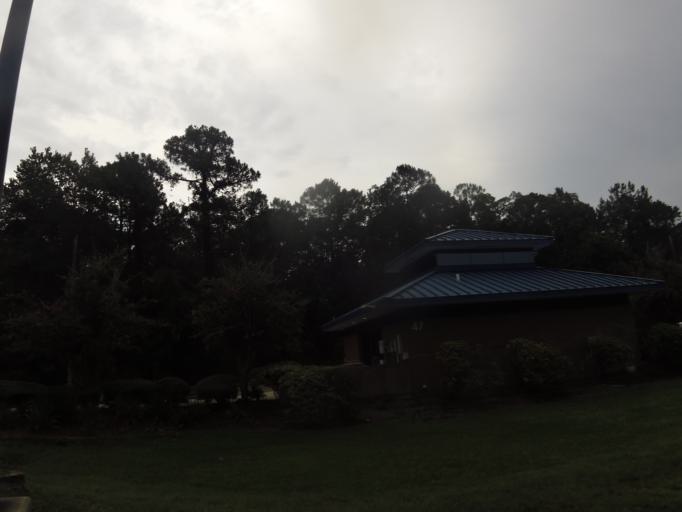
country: US
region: Florida
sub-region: Duval County
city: Jacksonville Beach
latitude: 30.2640
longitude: -81.5056
